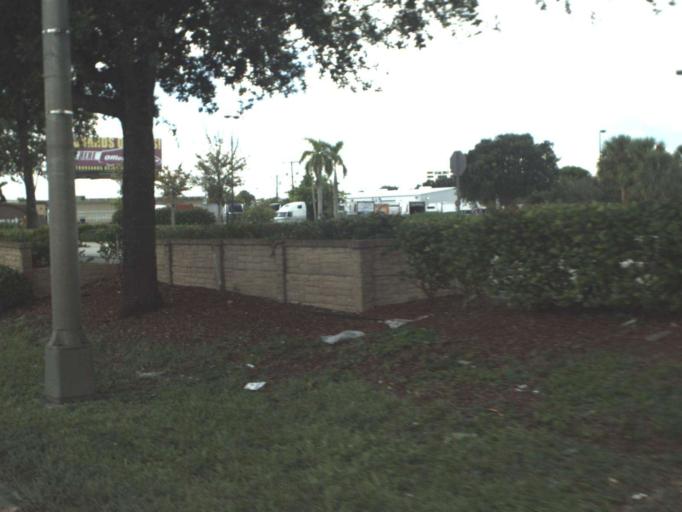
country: US
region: Florida
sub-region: Miami-Dade County
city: Norland
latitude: 25.9361
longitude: -80.2050
